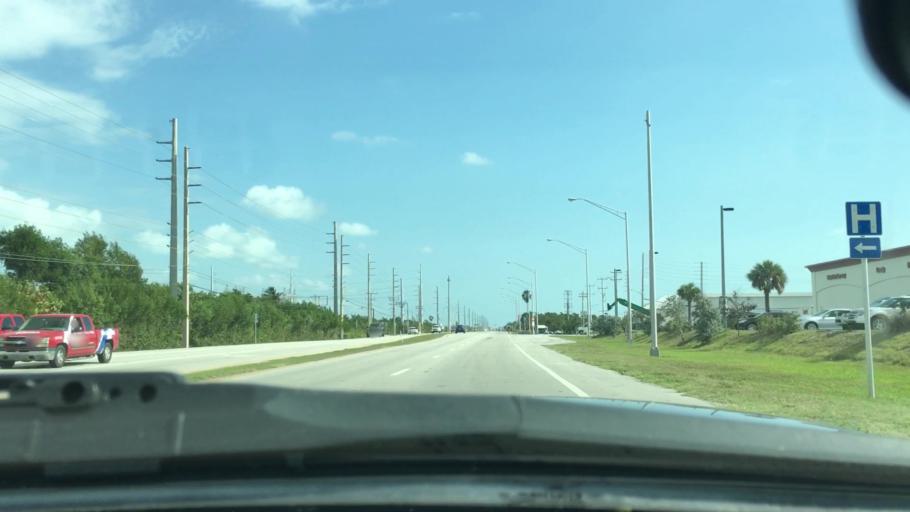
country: US
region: Florida
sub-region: Monroe County
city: Stock Island
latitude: 24.5744
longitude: -81.7374
